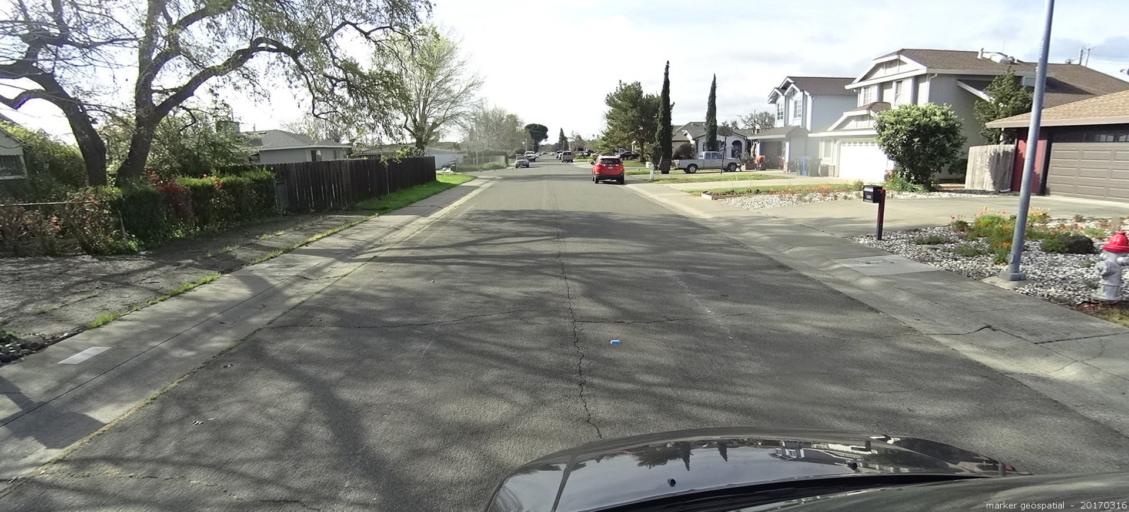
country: US
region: California
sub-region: Sacramento County
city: Parkway
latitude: 38.5143
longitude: -121.4818
